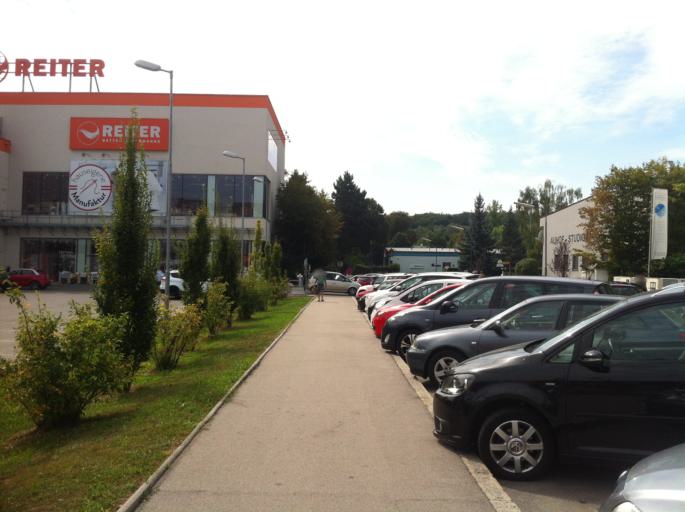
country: AT
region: Lower Austria
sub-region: Politischer Bezirk Wien-Umgebung
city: Purkersdorf
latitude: 48.2077
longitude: 16.2164
